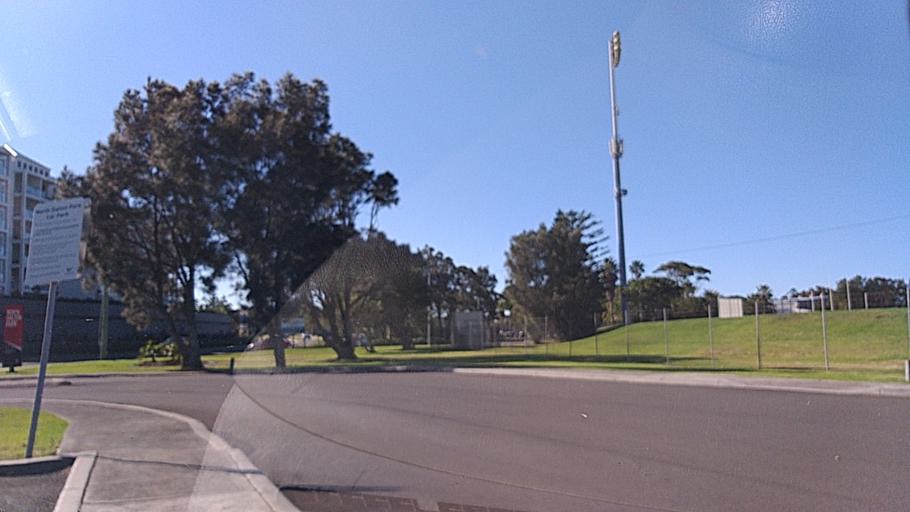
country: AU
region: New South Wales
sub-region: Wollongong
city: Fairy Meadow
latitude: -34.3909
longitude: 150.9037
